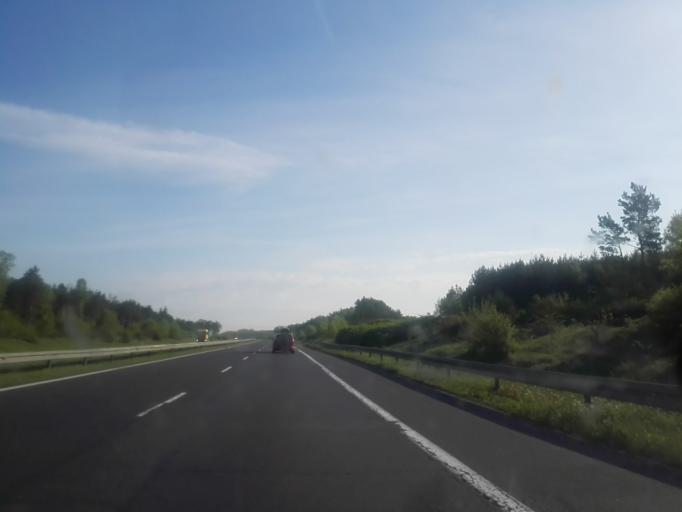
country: PL
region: Lodz Voivodeship
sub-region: Powiat radomszczanski
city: Kamiensk
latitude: 51.2421
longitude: 19.5217
